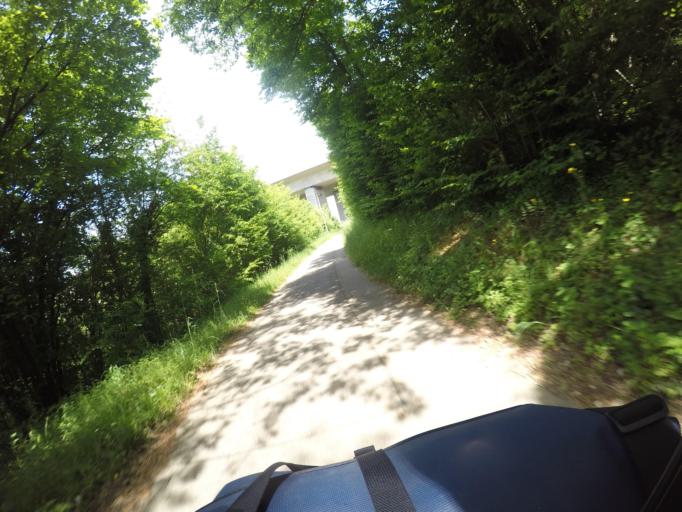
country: DE
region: Baden-Wuerttemberg
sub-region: Karlsruhe Region
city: Ispringen
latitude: 48.9078
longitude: 8.6856
